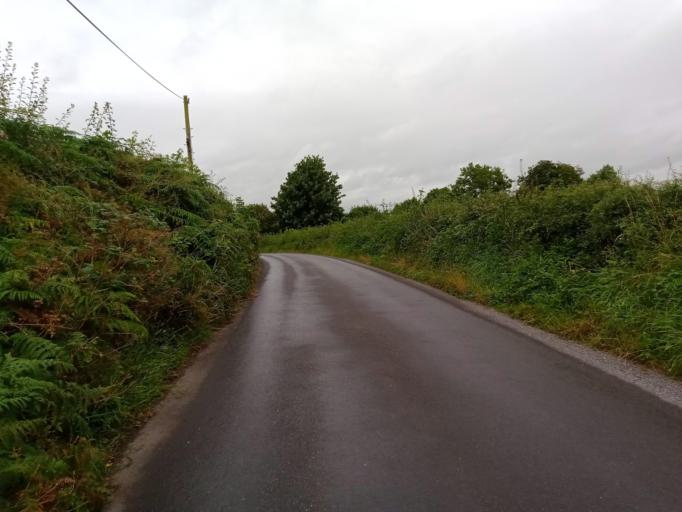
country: IE
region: Leinster
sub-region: Kilkenny
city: Ballyragget
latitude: 52.8102
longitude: -7.4354
